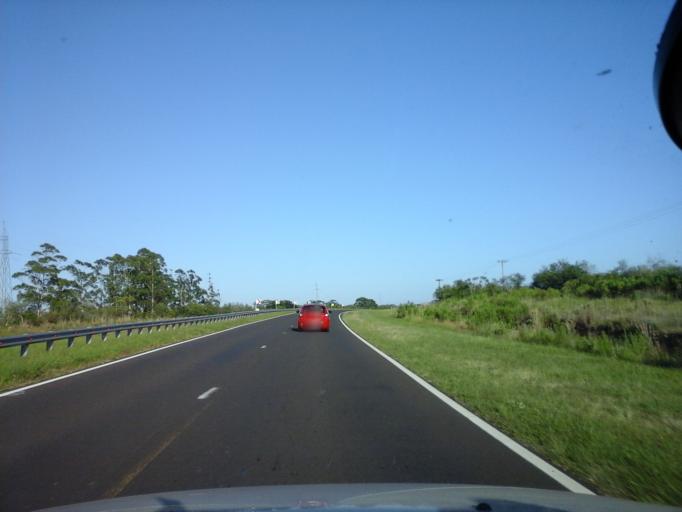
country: AR
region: Corrientes
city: Ita Ibate
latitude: -27.4858
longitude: -57.2858
